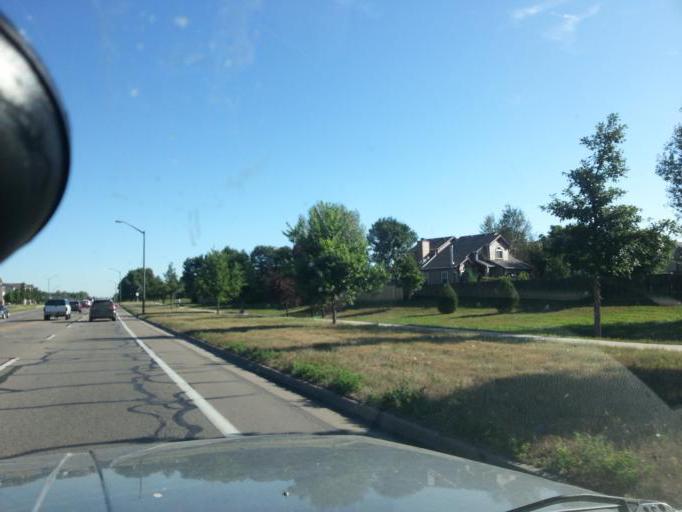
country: US
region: Colorado
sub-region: Larimer County
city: Fort Collins
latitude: 40.5267
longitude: -105.0393
